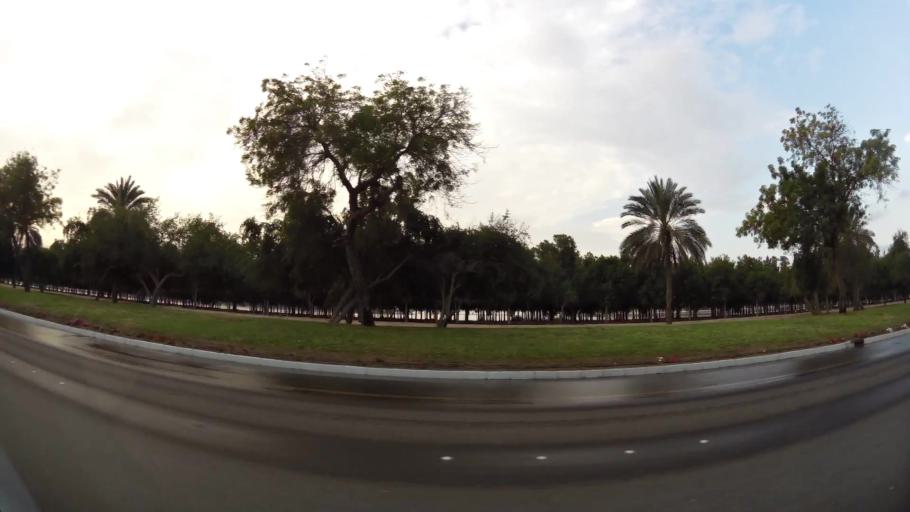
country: AE
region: Abu Dhabi
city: Abu Dhabi
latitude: 24.4114
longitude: 54.4567
